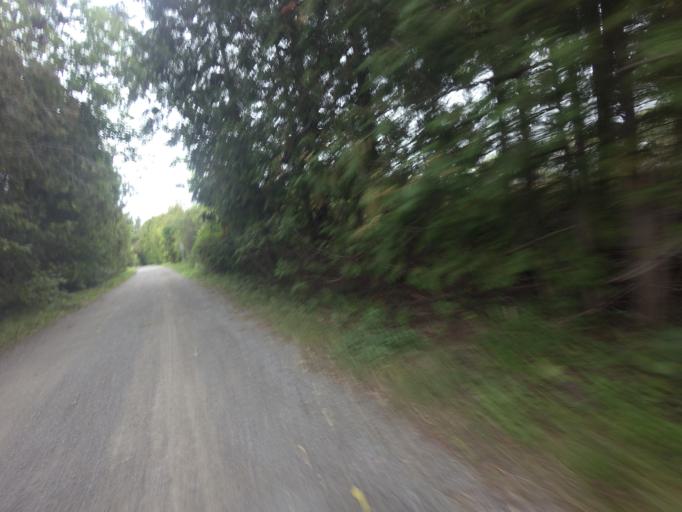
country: CA
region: Ontario
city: Omemee
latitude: 44.3815
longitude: -78.7514
